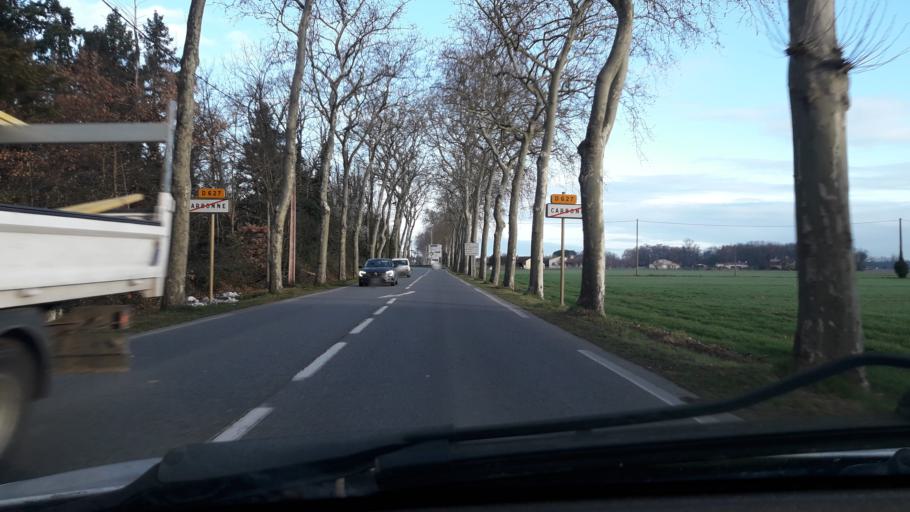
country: FR
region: Midi-Pyrenees
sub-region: Departement de la Haute-Garonne
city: Carbonne
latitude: 43.3151
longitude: 1.2211
